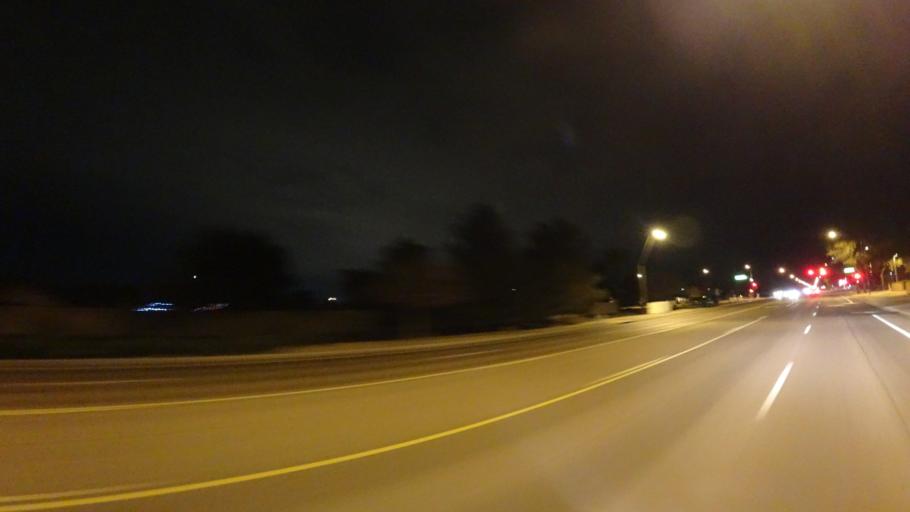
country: US
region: Arizona
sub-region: Maricopa County
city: Gilbert
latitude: 33.3491
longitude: -111.7384
